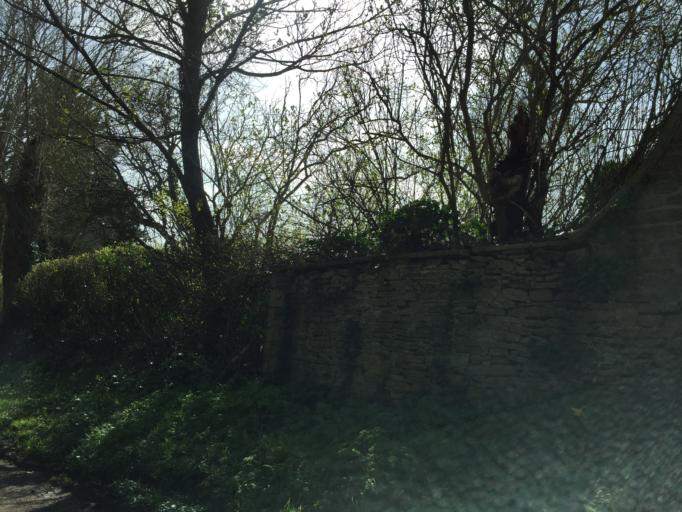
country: GB
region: England
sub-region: Wiltshire
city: Chippenham
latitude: 51.4730
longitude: -2.1501
